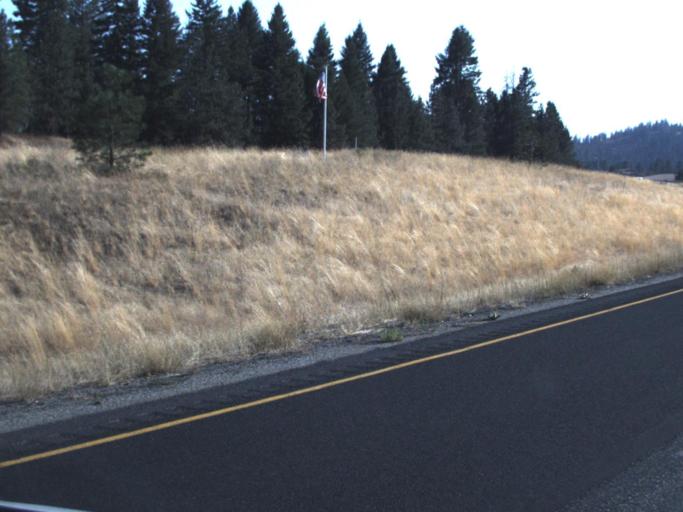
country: US
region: Washington
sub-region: Spokane County
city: Deer Park
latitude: 48.0640
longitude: -117.3434
